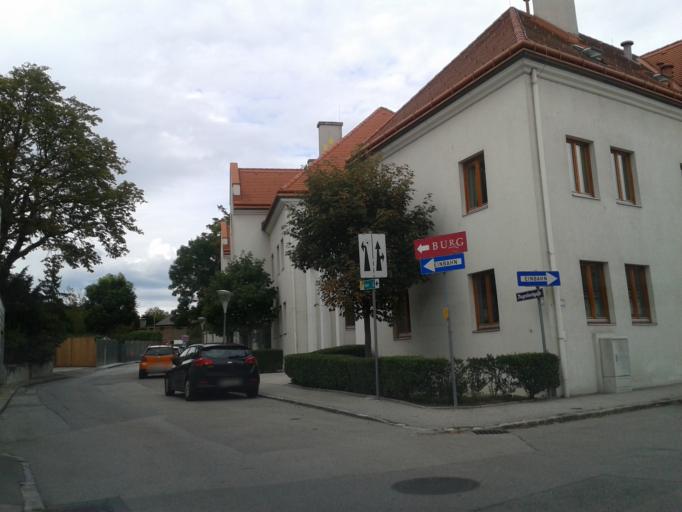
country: AT
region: Lower Austria
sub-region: Politischer Bezirk Modling
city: Perchtoldsdorf
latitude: 48.1237
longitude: 16.2703
